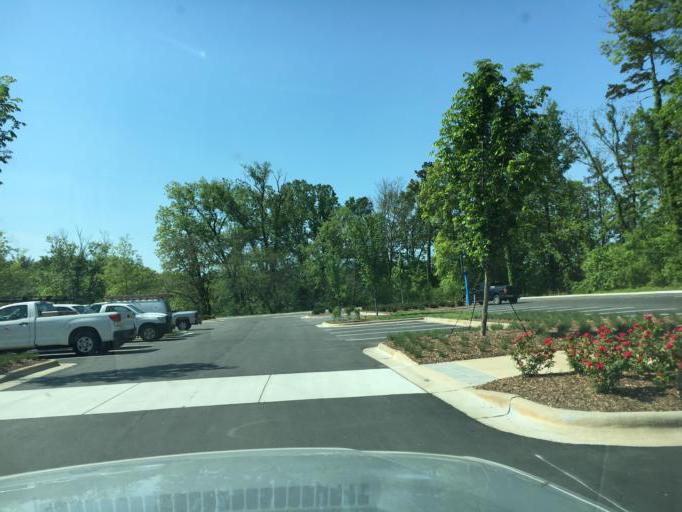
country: US
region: North Carolina
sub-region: Burke County
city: Morganton
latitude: 35.7336
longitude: -81.6803
